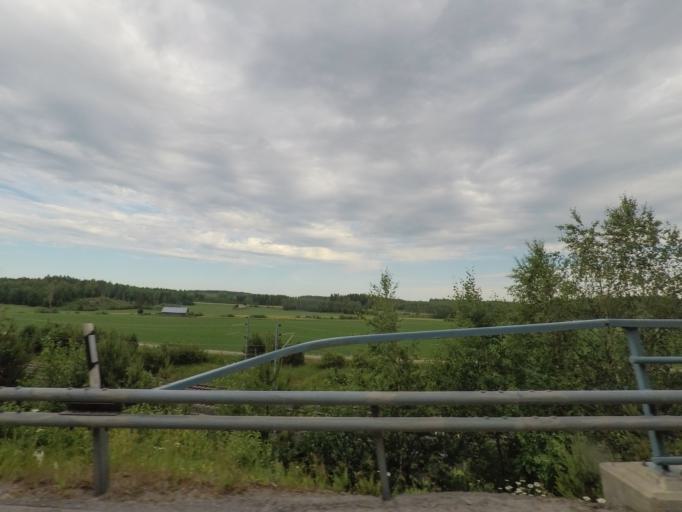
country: FI
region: Uusimaa
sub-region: Helsinki
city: Maentsaelae
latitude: 60.6803
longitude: 25.3603
